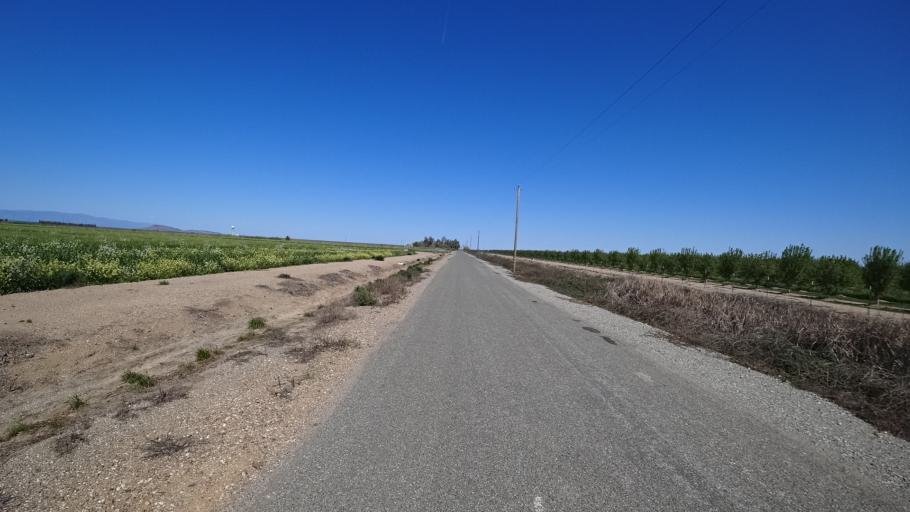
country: US
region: California
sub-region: Glenn County
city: Orland
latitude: 39.6708
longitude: -122.2344
